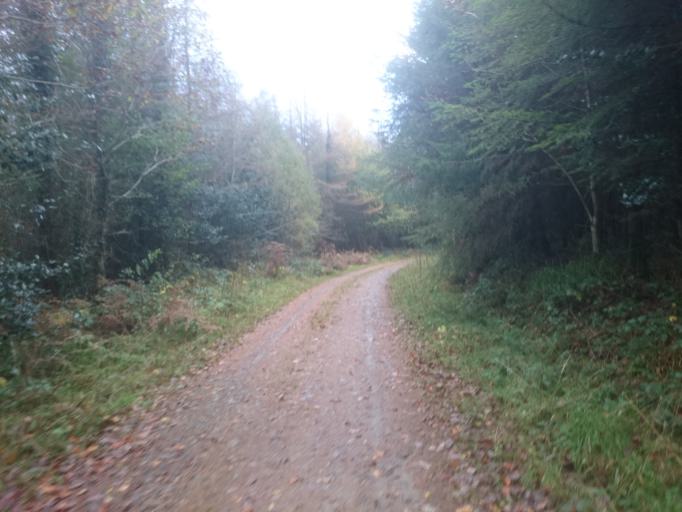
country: IE
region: Leinster
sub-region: Kilkenny
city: Thomastown
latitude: 52.4674
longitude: -7.0498
